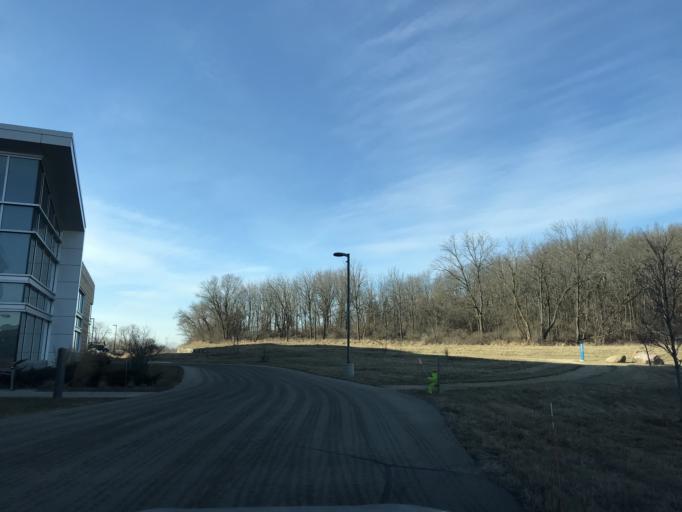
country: US
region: Wisconsin
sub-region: Dane County
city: Windsor
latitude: 43.1558
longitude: -89.3014
